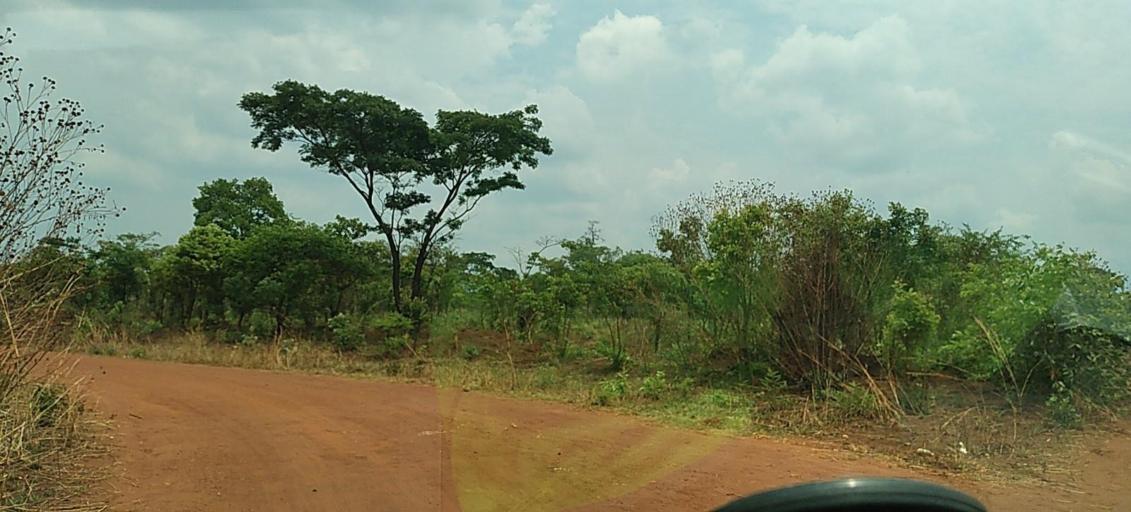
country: ZM
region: North-Western
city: Kansanshi
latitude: -12.0432
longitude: 26.3875
